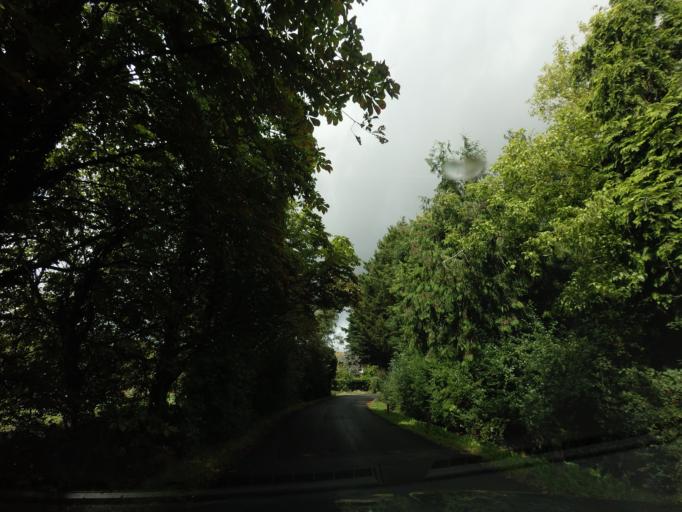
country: GB
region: England
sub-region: Kent
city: Paddock Wood
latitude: 51.1837
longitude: 0.4044
